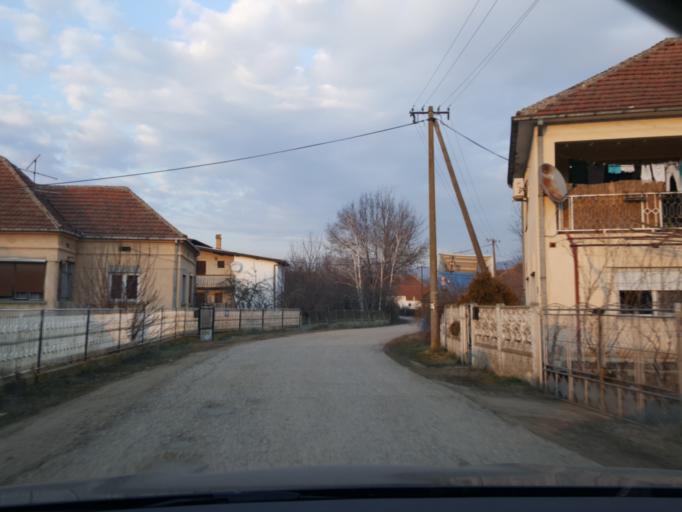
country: RS
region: Central Serbia
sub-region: Nisavski Okrug
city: Aleksinac
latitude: 43.5729
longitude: 21.6433
